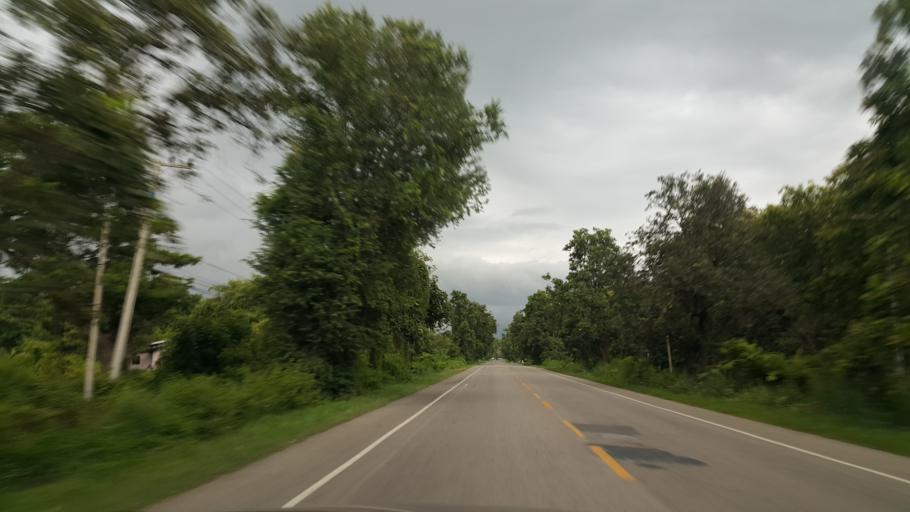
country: TH
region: Phayao
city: Dok Kham Tai
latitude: 19.2134
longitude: 100.0390
